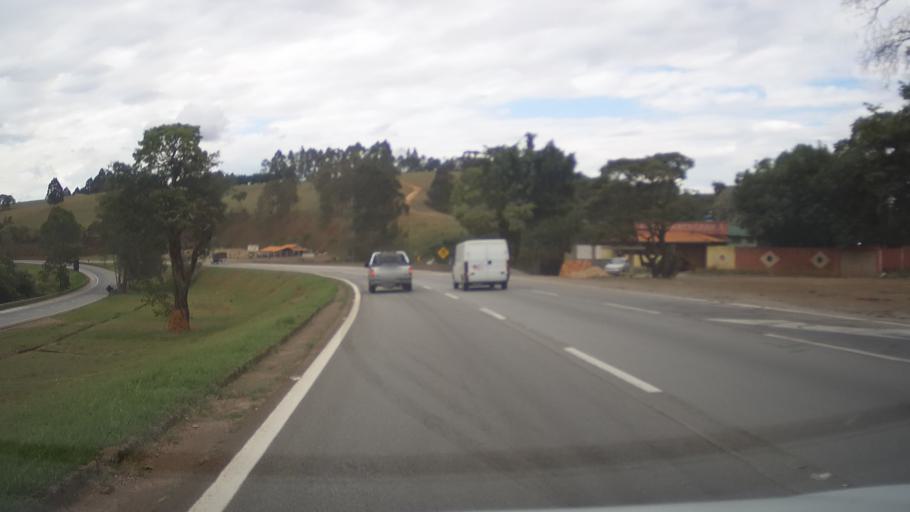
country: BR
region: Minas Gerais
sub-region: Itauna
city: Itauna
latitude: -20.3410
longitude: -44.4409
